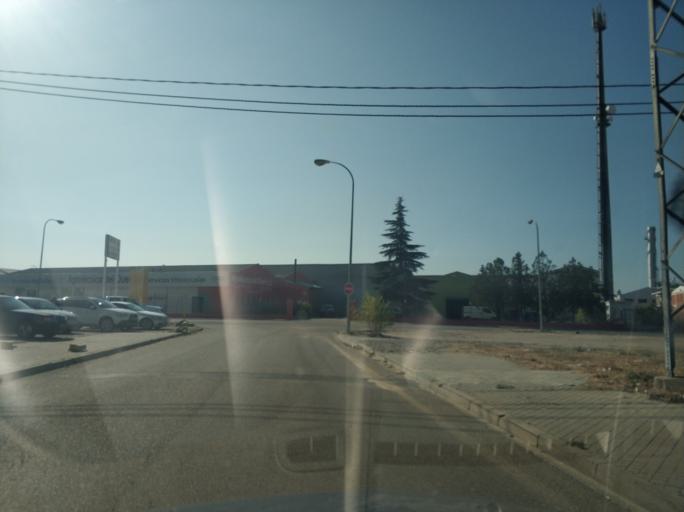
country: ES
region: Castille and Leon
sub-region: Provincia de Burgos
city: Aranda de Duero
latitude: 41.6671
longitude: -3.7092
